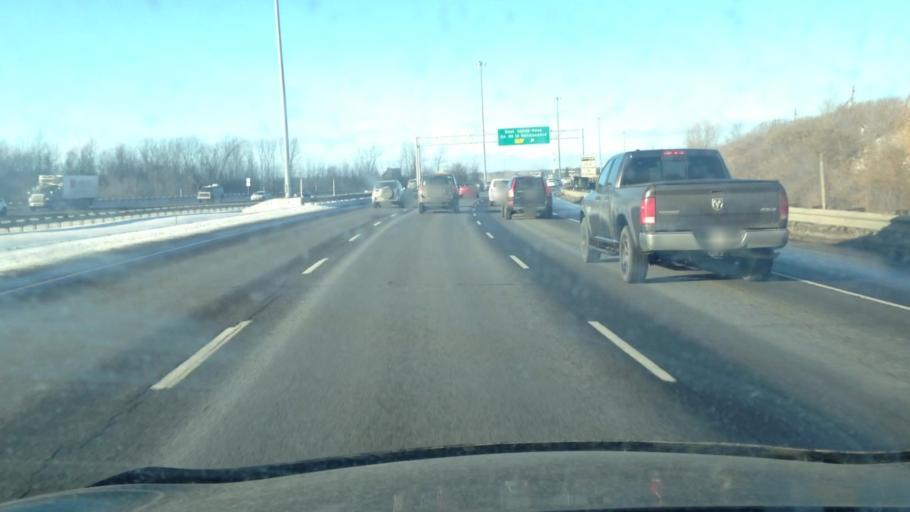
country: CA
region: Quebec
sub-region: Laurentides
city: Boisbriand
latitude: 45.5933
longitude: -73.8020
